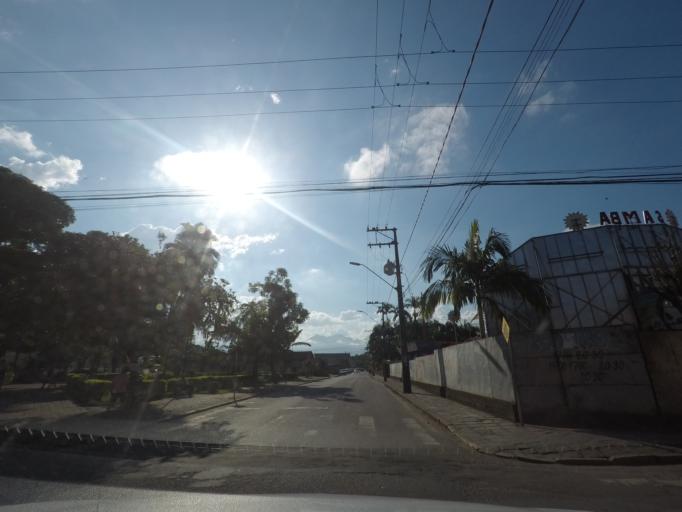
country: BR
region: Parana
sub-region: Antonina
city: Antonina
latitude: -25.4796
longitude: -48.8327
